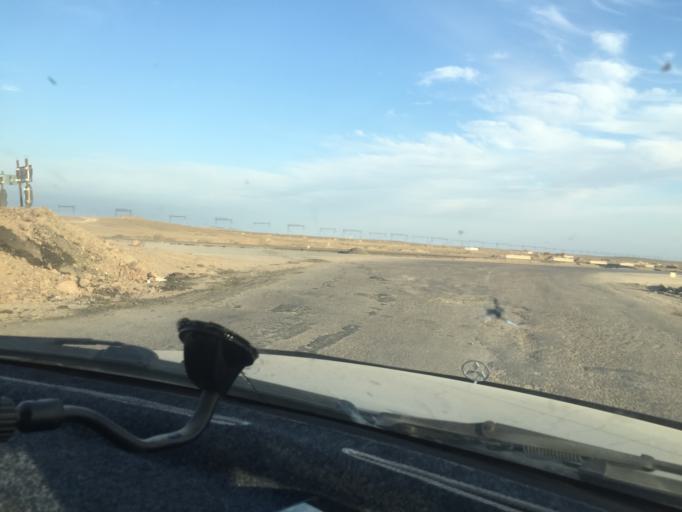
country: KZ
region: Almaty Oblysy
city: Ulken
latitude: 45.2420
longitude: 73.8248
